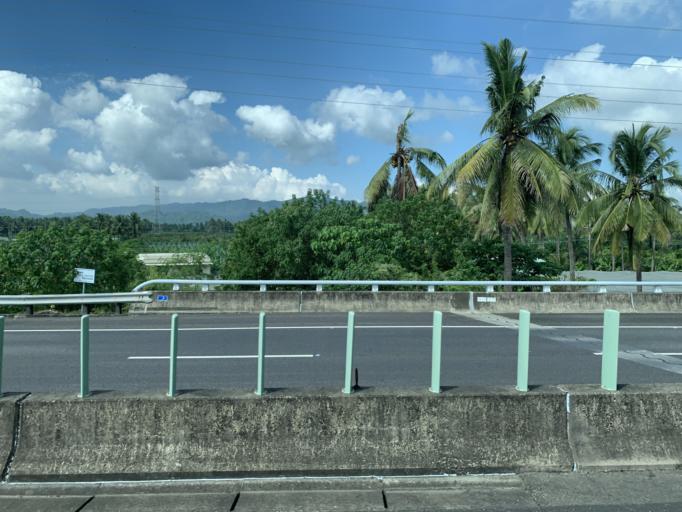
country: TW
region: Taiwan
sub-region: Pingtung
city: Pingtung
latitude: 22.8436
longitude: 120.4960
